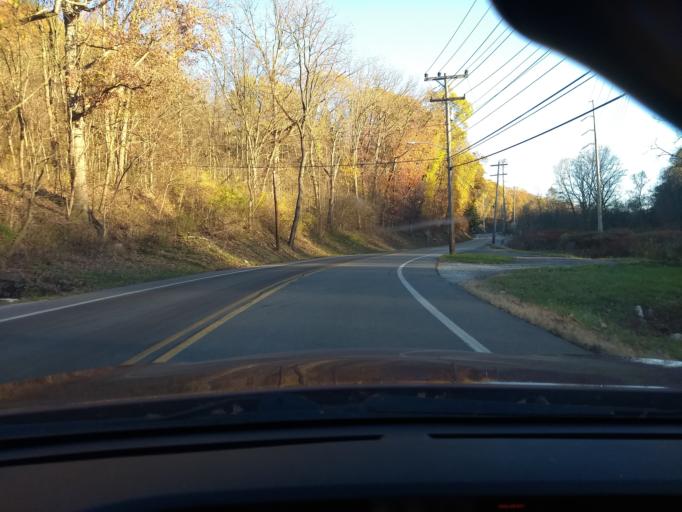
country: US
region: Pennsylvania
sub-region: Allegheny County
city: Upper Saint Clair
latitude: 40.3515
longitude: -80.0859
